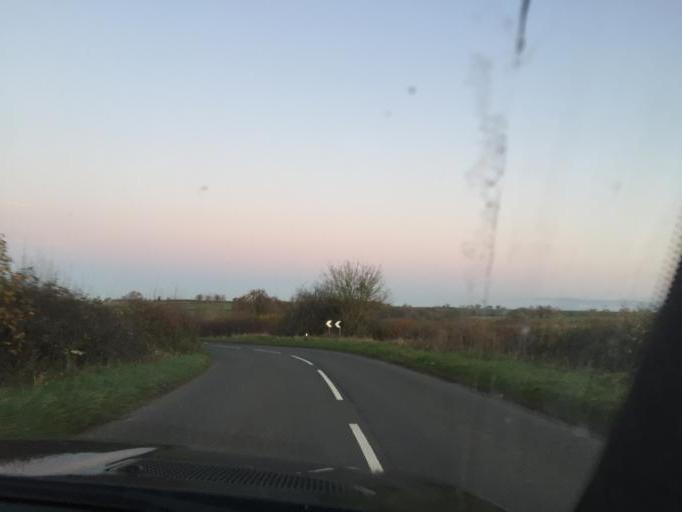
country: GB
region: England
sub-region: Northamptonshire
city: Brackley
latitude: 52.0944
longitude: -1.1226
